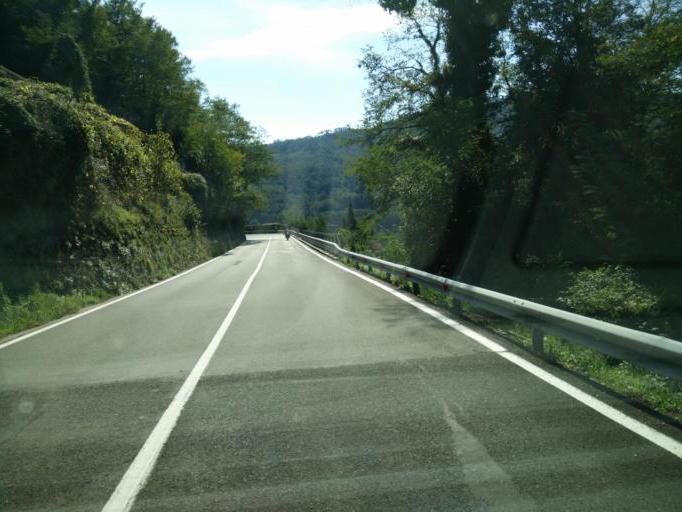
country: IT
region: Liguria
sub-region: Provincia di La Spezia
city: Carrodano
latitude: 44.2450
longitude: 9.6527
